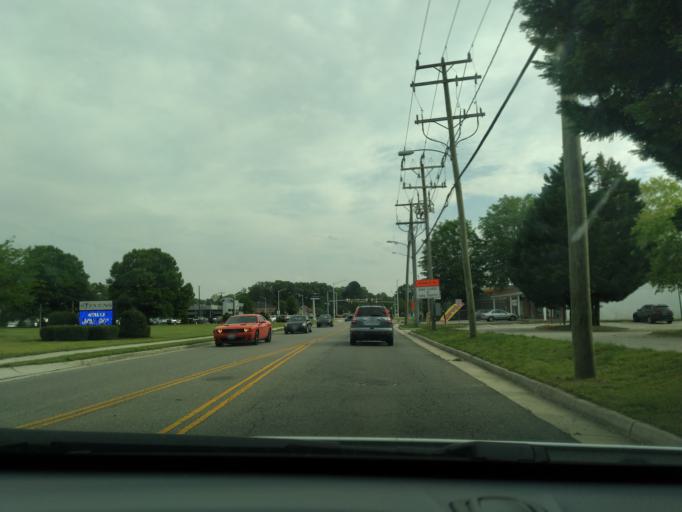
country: US
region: Virginia
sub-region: York County
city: Yorktown
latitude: 37.1506
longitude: -76.5278
